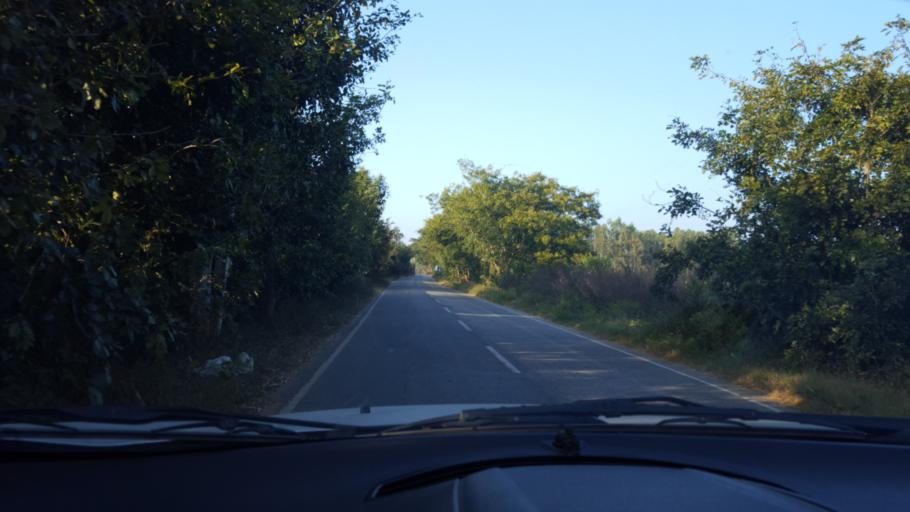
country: IN
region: Karnataka
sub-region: Bangalore Urban
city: Yelahanka
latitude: 13.1763
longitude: 77.5992
